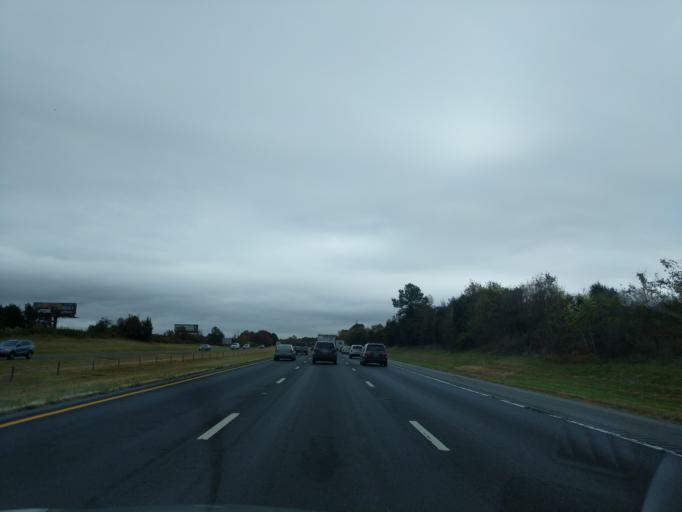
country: US
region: North Carolina
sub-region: Davidson County
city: Thomasville
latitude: 35.8594
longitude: -80.0657
